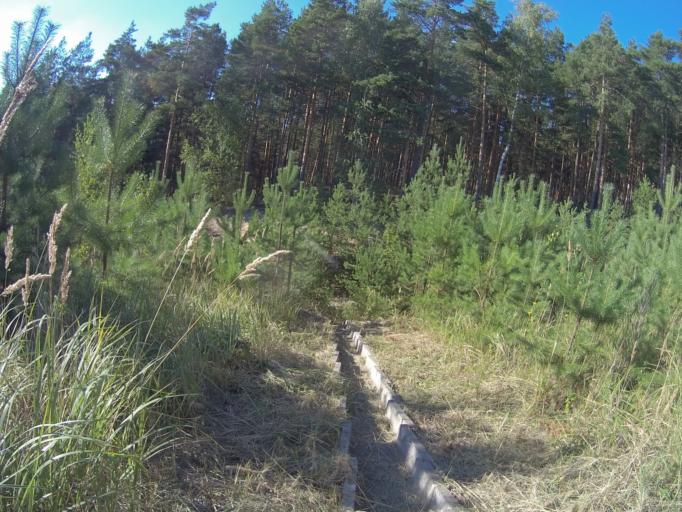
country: RU
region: Vladimir
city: Kommunar
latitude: 56.0561
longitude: 40.4366
